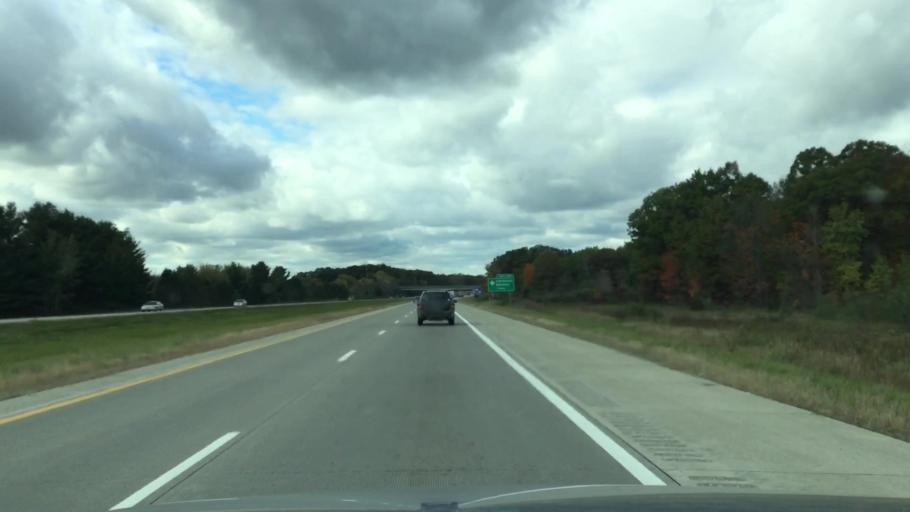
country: US
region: Michigan
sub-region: Genesee County
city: Davison
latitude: 43.0138
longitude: -83.4883
